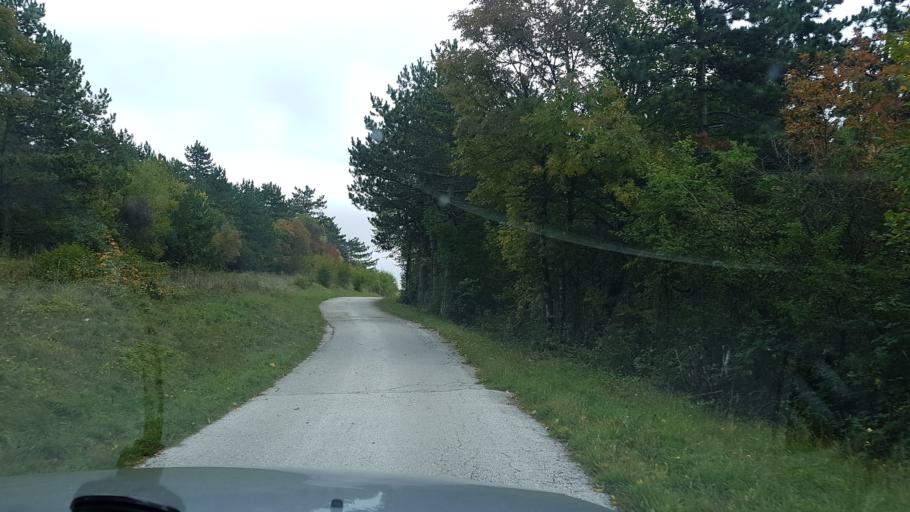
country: HR
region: Istarska
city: Buzet
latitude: 45.4495
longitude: 14.0220
